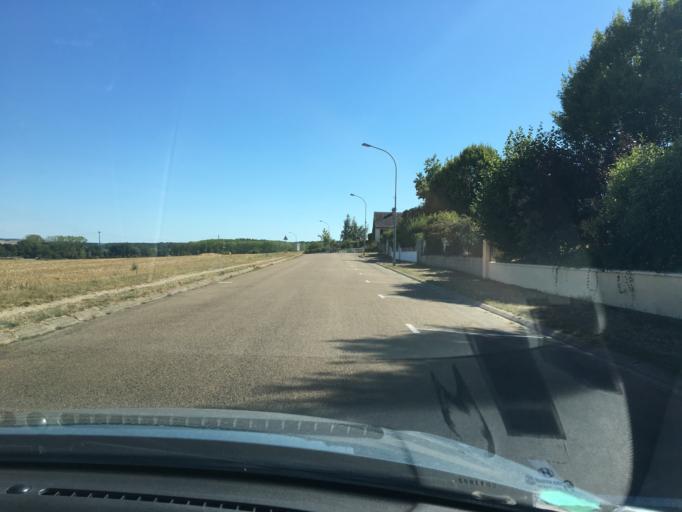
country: FR
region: Bourgogne
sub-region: Departement de l'Yonne
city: Appoigny
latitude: 47.8712
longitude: 3.5206
